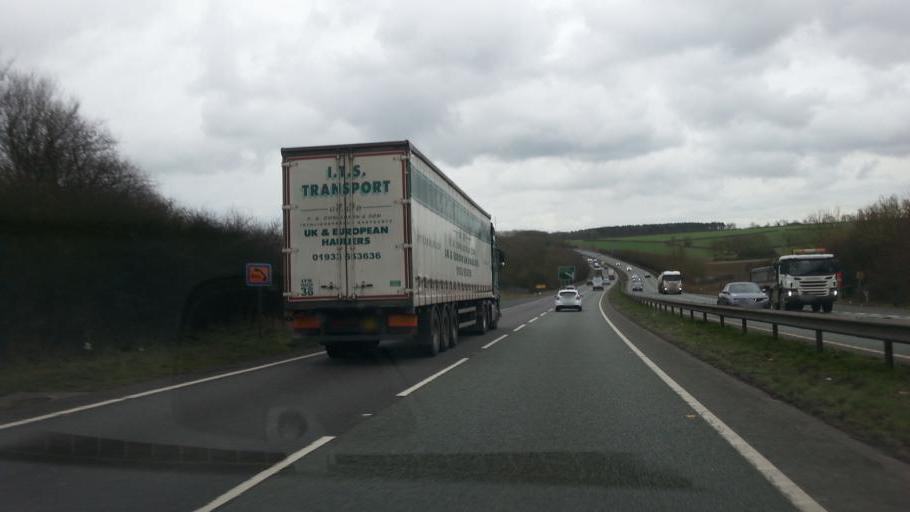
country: GB
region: England
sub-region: Leicestershire
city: Market Harborough
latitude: 52.4041
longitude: -0.9389
